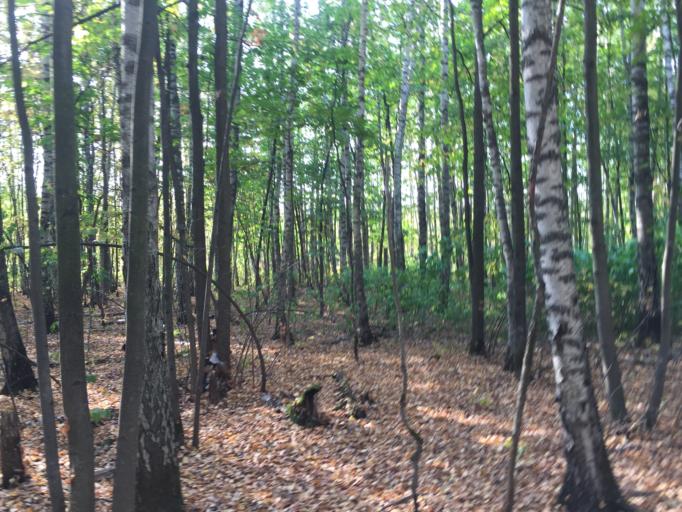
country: RU
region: Moscow
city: Babushkin
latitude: 55.8558
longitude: 37.7214
